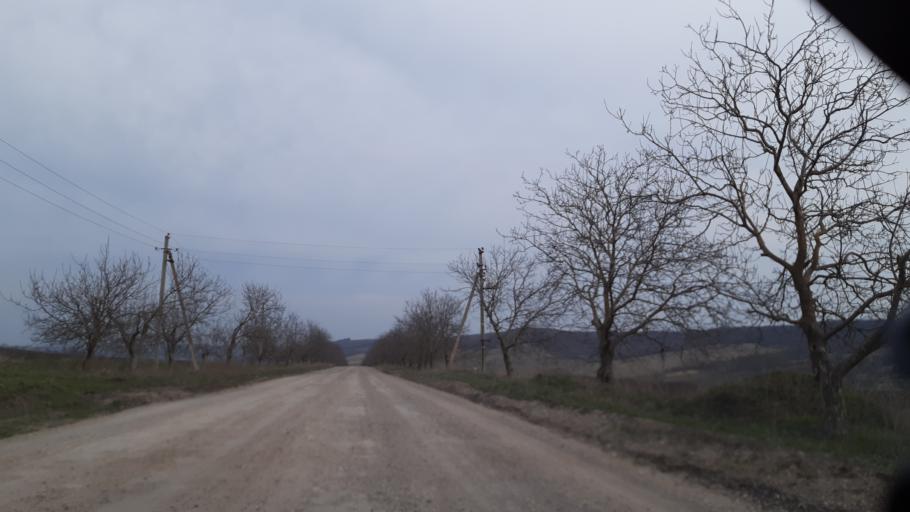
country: MD
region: Soldanesti
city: Soldanesti
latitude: 47.6924
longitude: 28.7375
